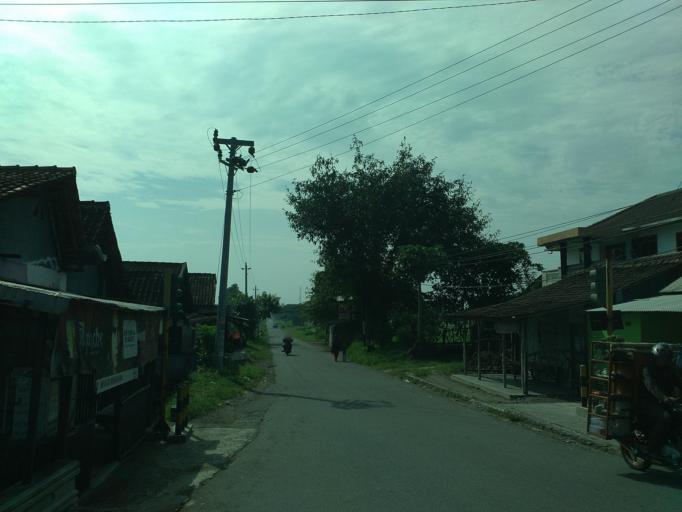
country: ID
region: Central Java
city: Ceper
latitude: -7.6640
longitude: 110.6674
